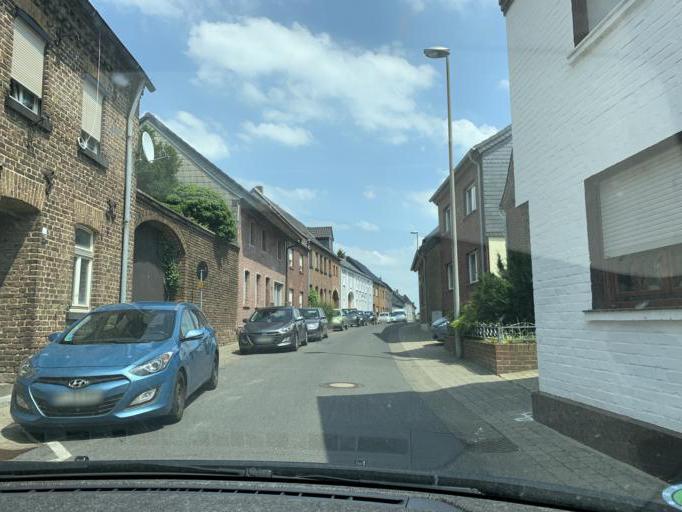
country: DE
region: North Rhine-Westphalia
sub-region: Regierungsbezirk Koln
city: Bedburg
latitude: 50.9828
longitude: 6.5174
